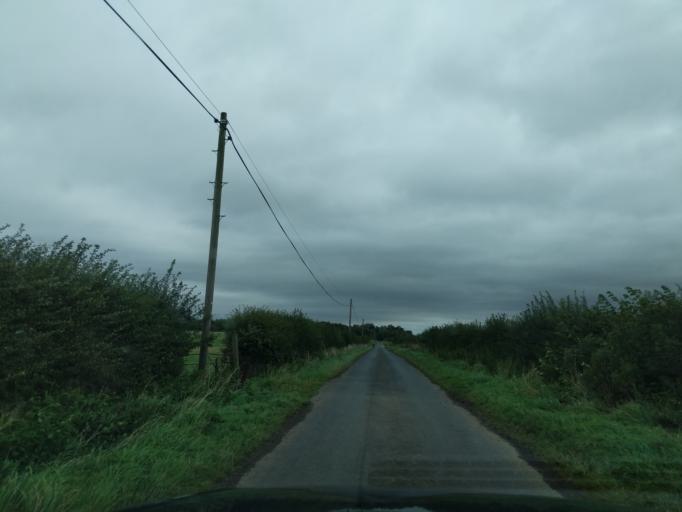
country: GB
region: Scotland
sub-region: The Scottish Borders
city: Kelso
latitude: 55.6023
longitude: -2.5075
